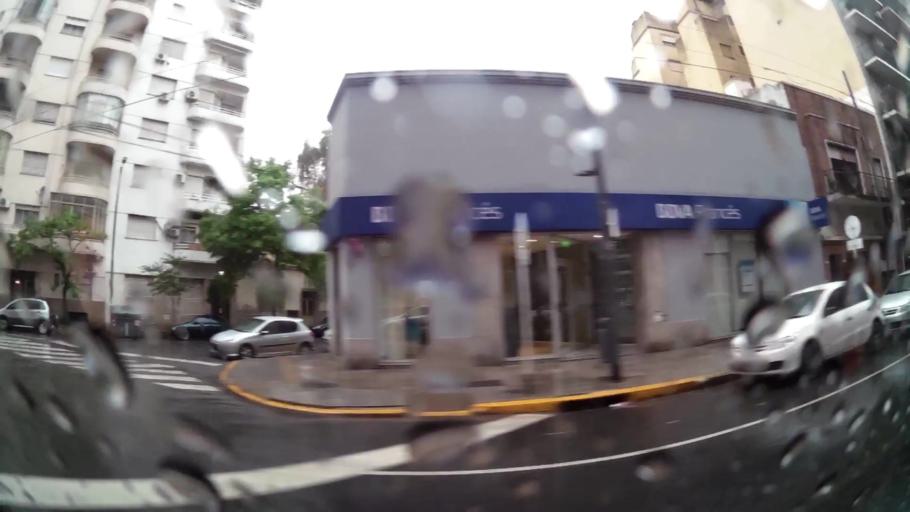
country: AR
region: Buenos Aires F.D.
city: Buenos Aires
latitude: -34.6328
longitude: -58.3741
